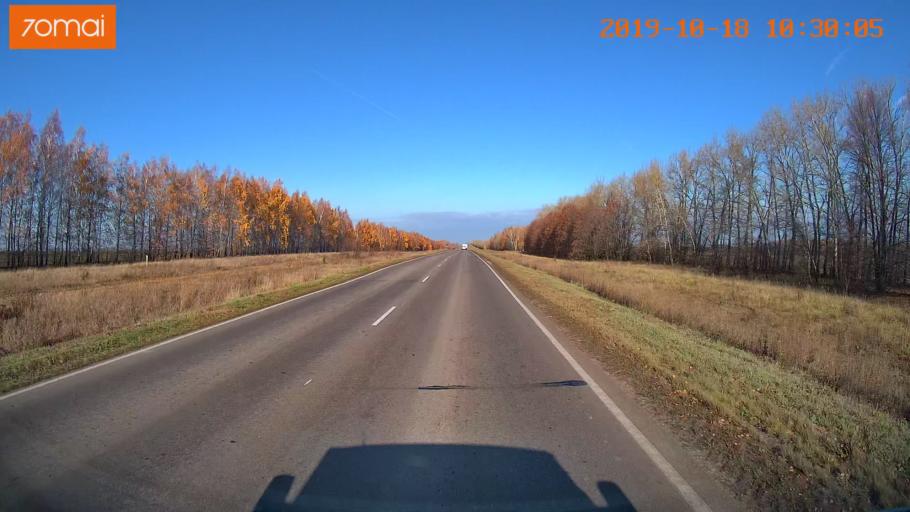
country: RU
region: Tula
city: Kurkino
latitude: 53.4605
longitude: 38.6484
